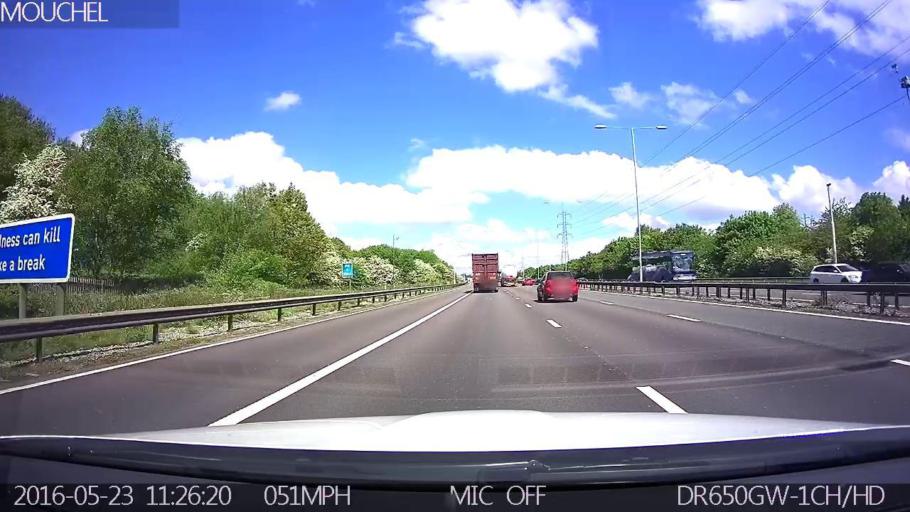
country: GB
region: England
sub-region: Walsall
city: Bloxwich
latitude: 52.6023
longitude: -2.0177
